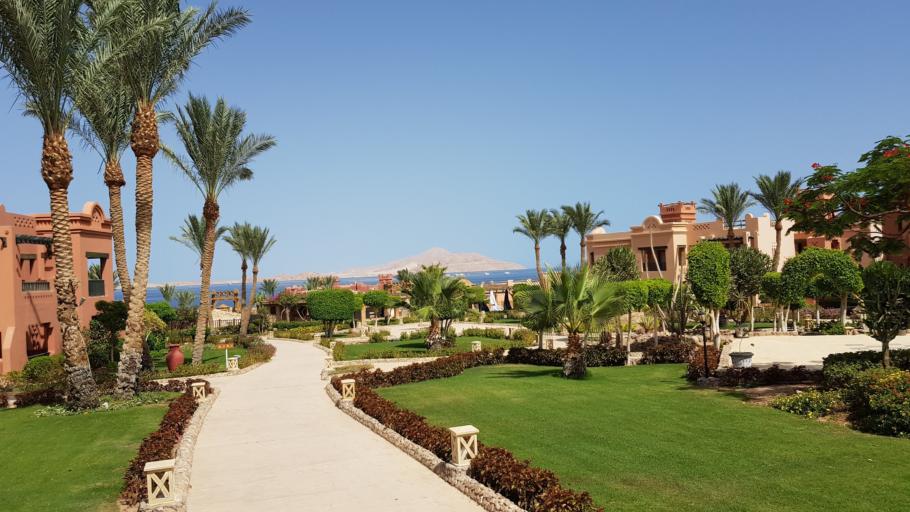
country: EG
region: South Sinai
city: Sharm el-Sheikh
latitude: 27.9976
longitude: 34.4322
